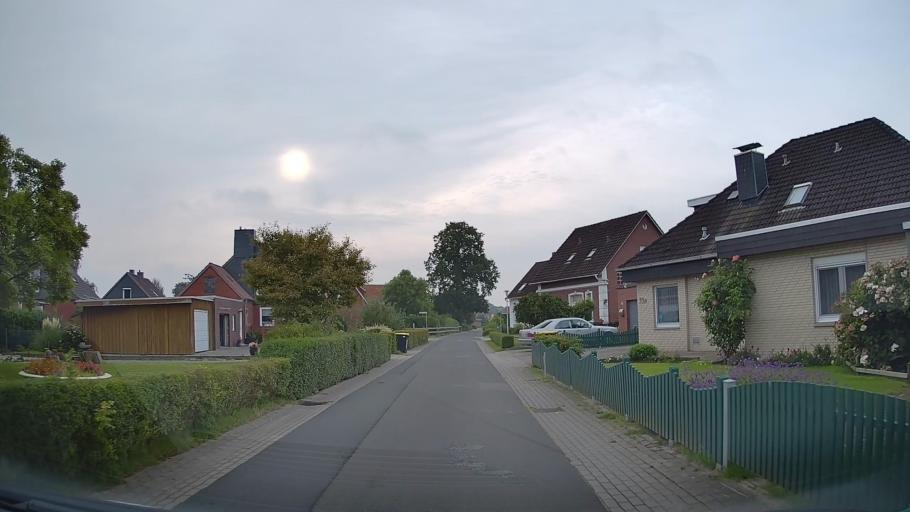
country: DE
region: Lower Saxony
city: Cuxhaven
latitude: 53.8289
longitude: 8.7651
